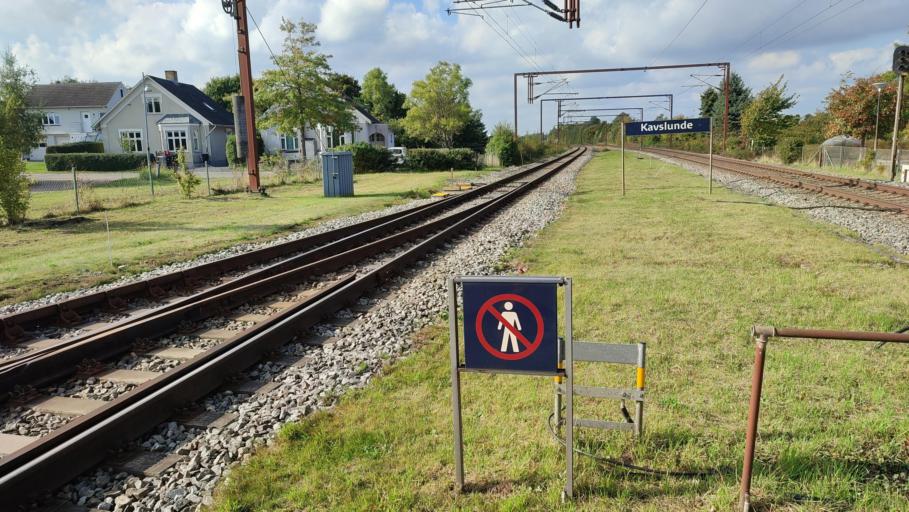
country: DK
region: South Denmark
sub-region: Middelfart Kommune
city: Norre Aby
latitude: 55.4760
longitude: 9.8102
